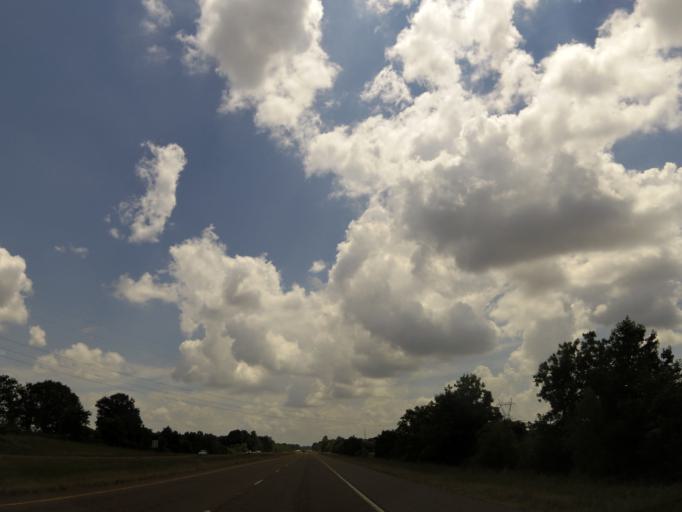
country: US
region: Tennessee
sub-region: Dyer County
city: Dyersburg
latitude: 36.0112
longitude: -89.3414
